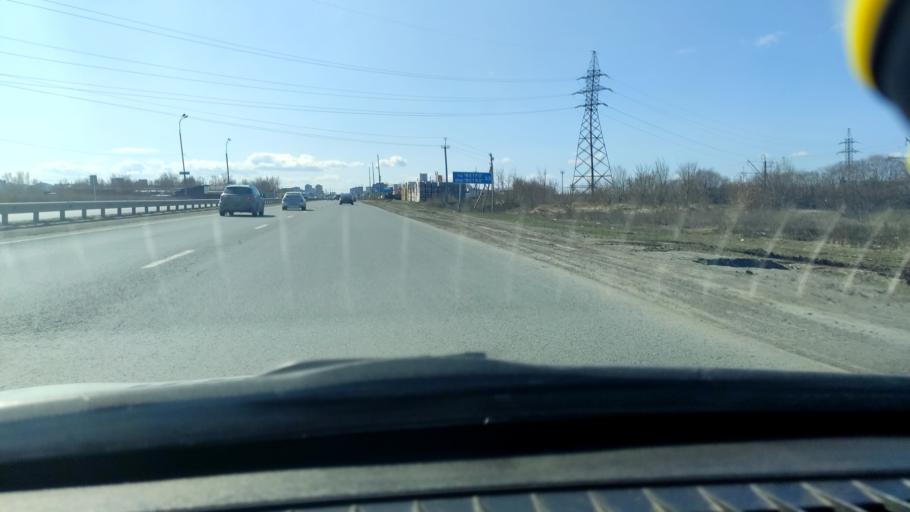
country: RU
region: Samara
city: Tol'yatti
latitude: 53.5633
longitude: 49.3638
